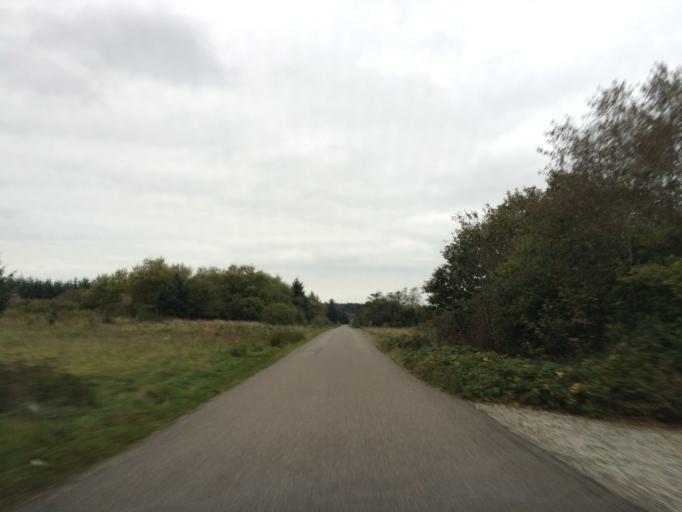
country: DK
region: Central Jutland
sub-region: Holstebro Kommune
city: Ulfborg
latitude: 56.2216
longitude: 8.4416
